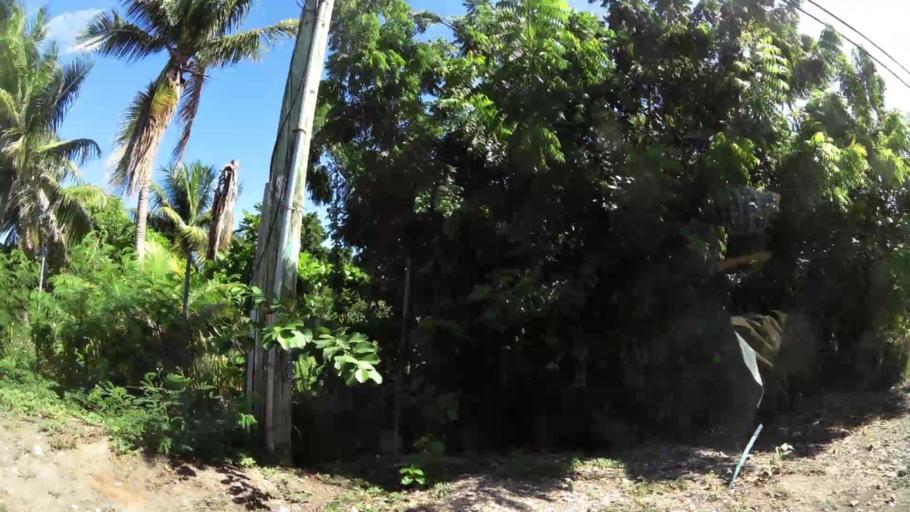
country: AG
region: Saint Paul
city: Falmouth
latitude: 17.0235
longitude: -61.7660
